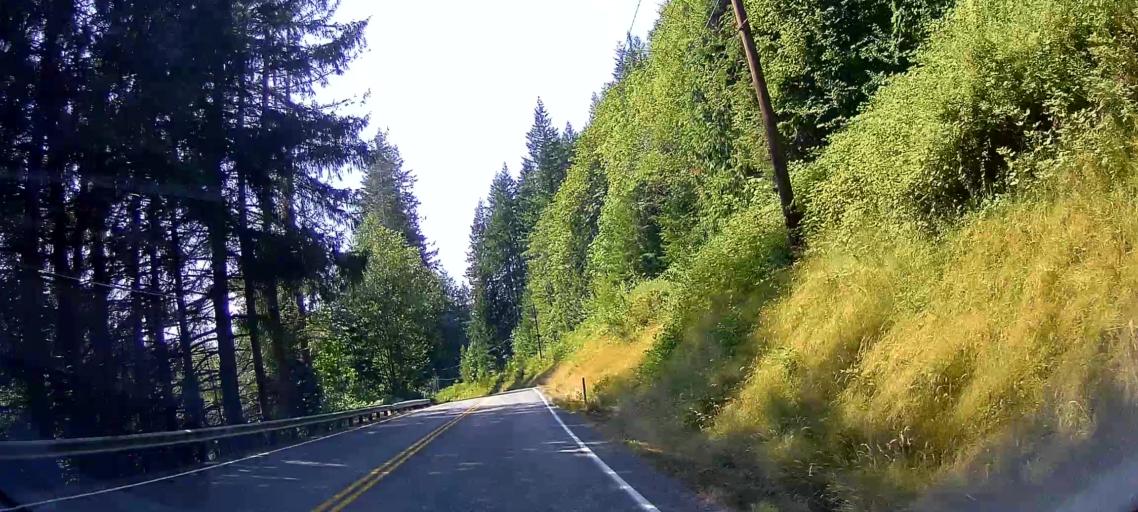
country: US
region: Washington
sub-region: Snohomish County
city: Bryant
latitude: 48.3267
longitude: -122.1447
